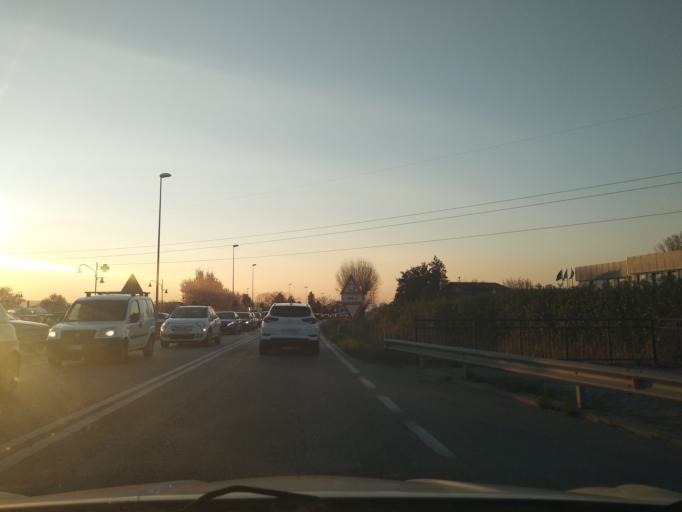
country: IT
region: Veneto
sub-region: Provincia di Padova
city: Mestrino
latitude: 45.4455
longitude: 11.7435
